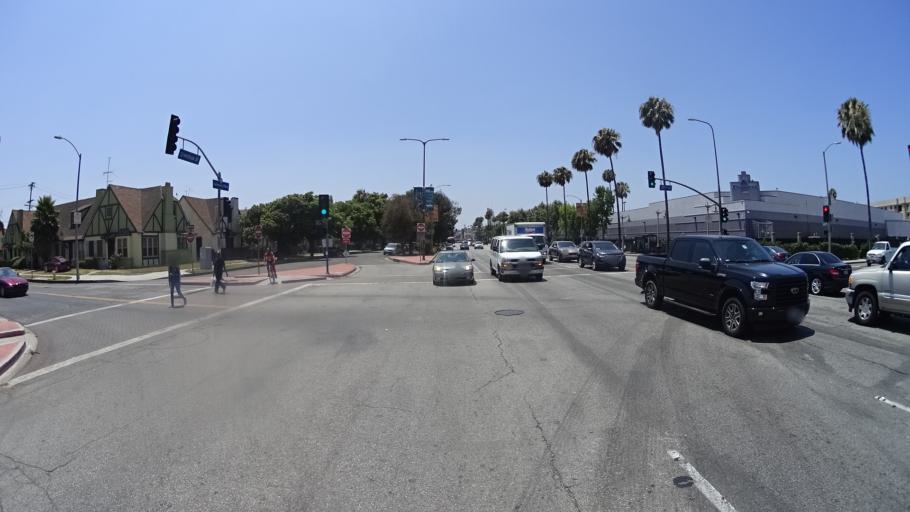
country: US
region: California
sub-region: Los Angeles County
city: View Park-Windsor Hills
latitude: 34.0147
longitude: -118.3351
